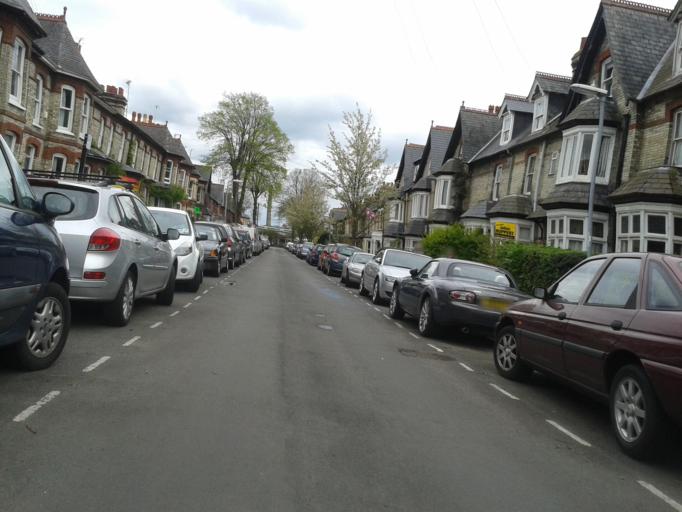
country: GB
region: England
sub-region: Cambridgeshire
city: Cambridge
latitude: 52.2135
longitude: 0.1334
